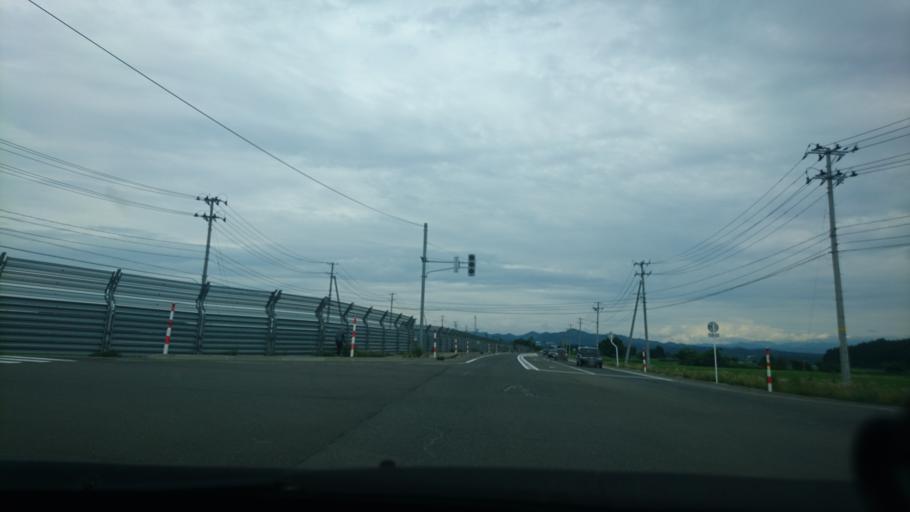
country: JP
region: Akita
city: Omagari
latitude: 39.5174
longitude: 140.3776
